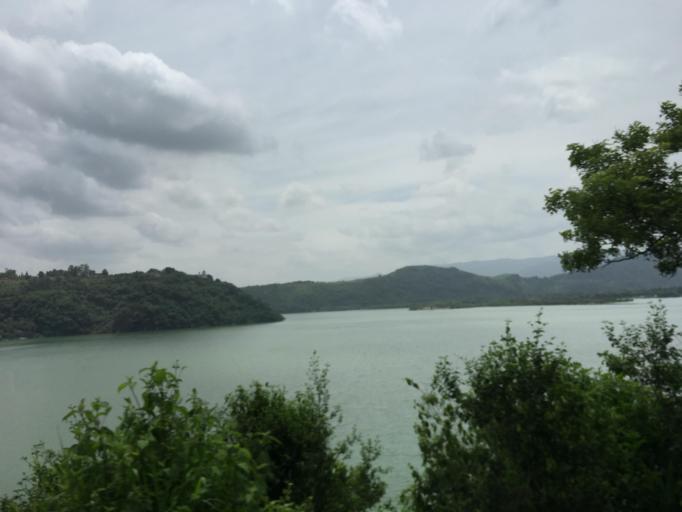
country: GT
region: Guatemala
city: Amatitlan
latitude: 14.4718
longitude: -90.5901
